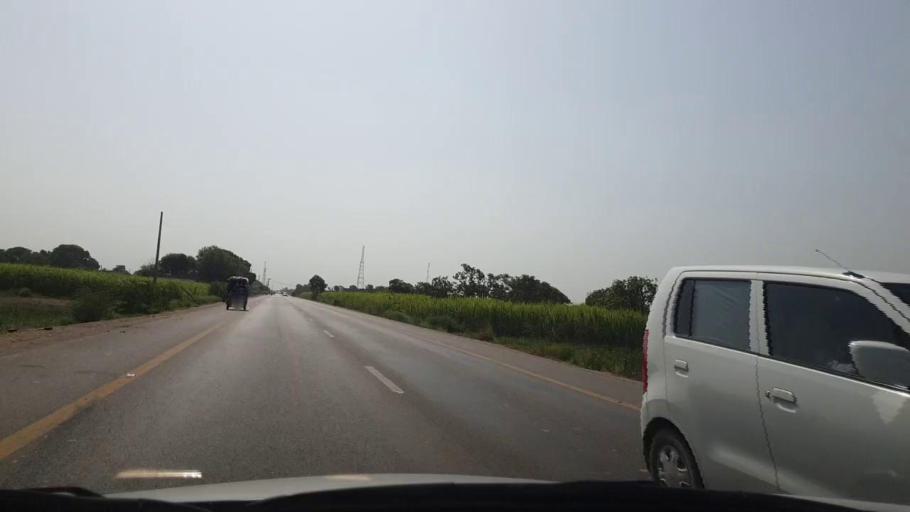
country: PK
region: Sindh
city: Tando Muhammad Khan
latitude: 25.0990
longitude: 68.5918
